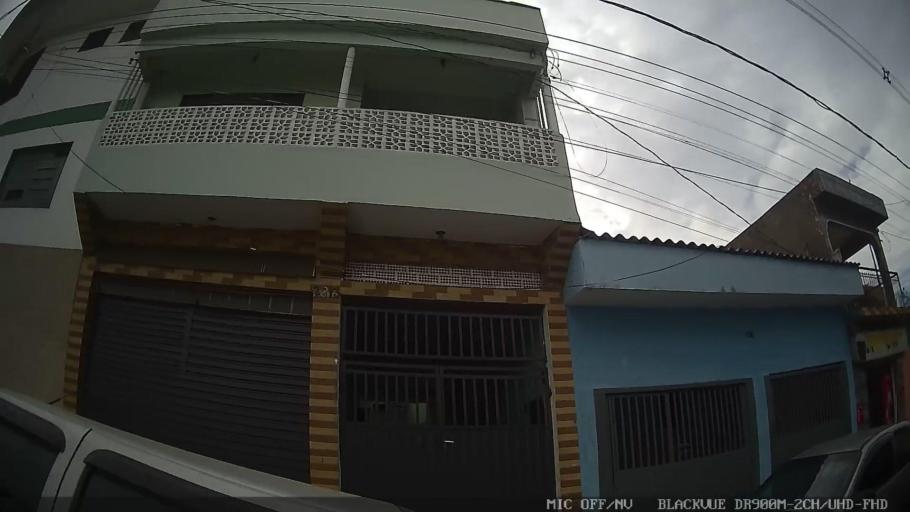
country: BR
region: Sao Paulo
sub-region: Salto
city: Salto
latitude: -23.1948
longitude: -47.2722
